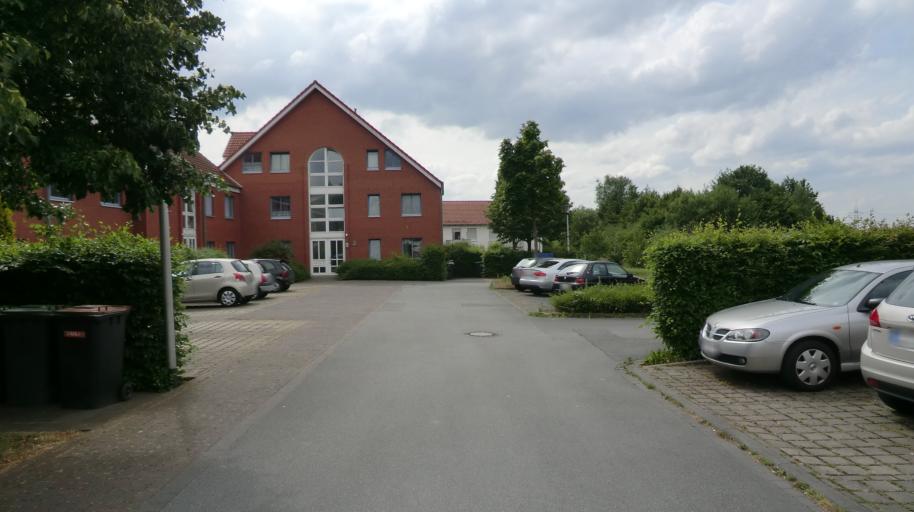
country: DE
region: North Rhine-Westphalia
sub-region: Regierungsbezirk Detmold
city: Hiddenhausen
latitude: 52.1554
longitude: 8.6407
